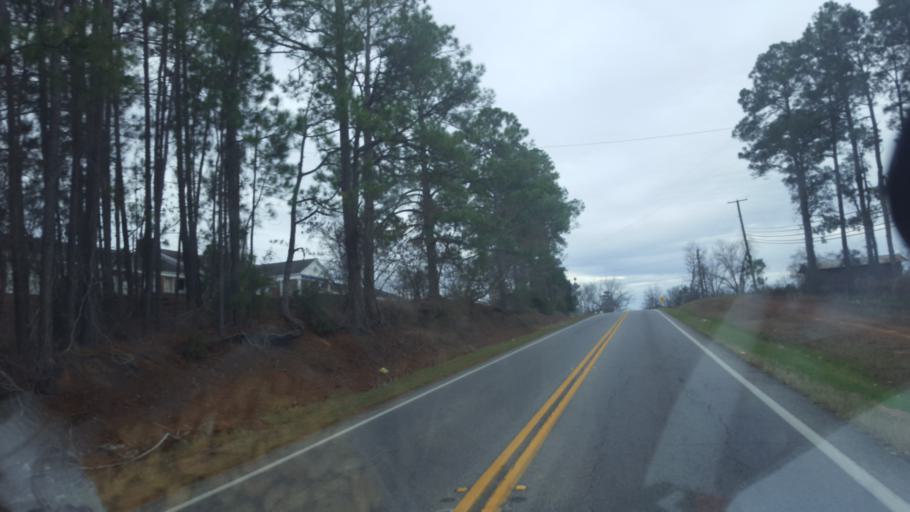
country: US
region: Georgia
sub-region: Ben Hill County
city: Fitzgerald
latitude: 31.7431
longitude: -83.2610
